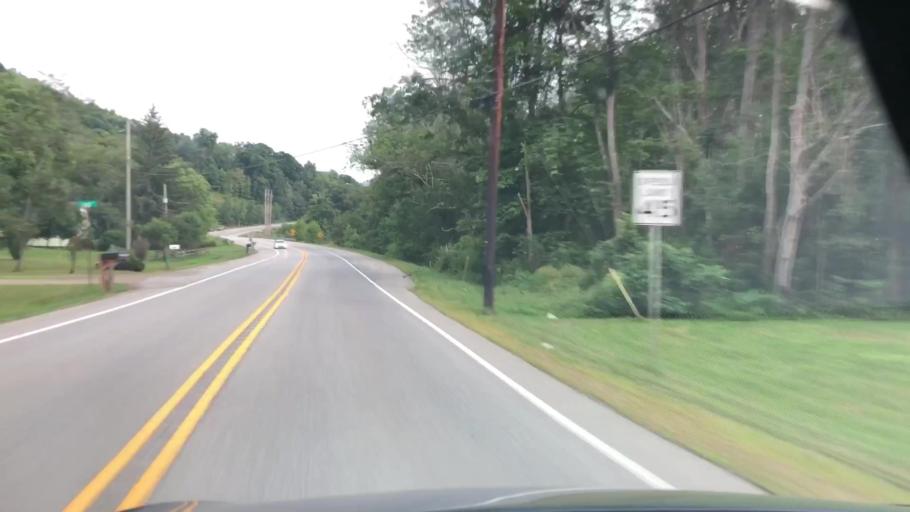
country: US
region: Pennsylvania
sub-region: Venango County
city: Hasson Heights
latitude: 41.4805
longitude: -79.6936
